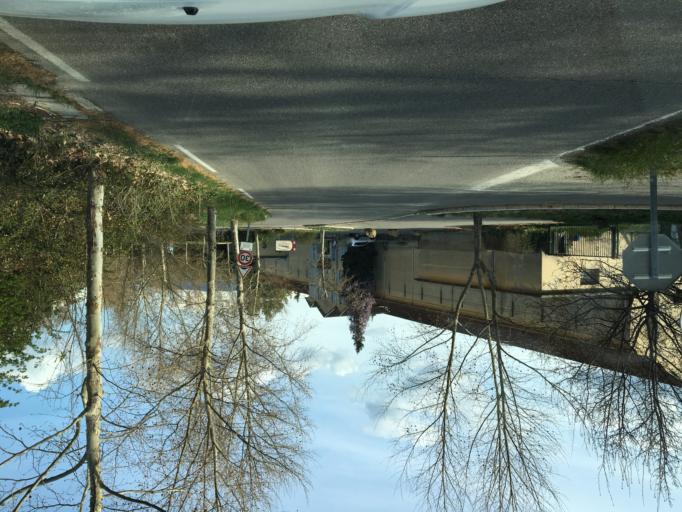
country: FR
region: Provence-Alpes-Cote d'Azur
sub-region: Departement du Vaucluse
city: Ansouis
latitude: 43.7375
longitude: 5.4605
